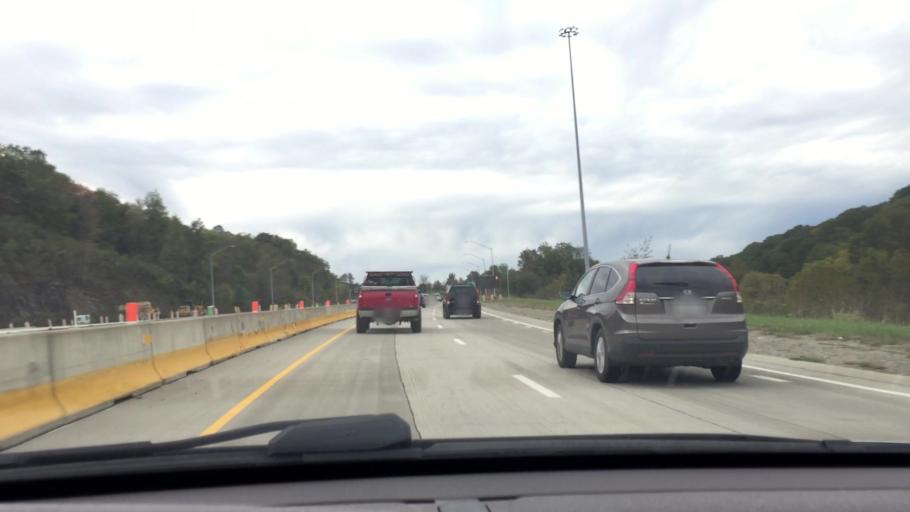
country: US
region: Pennsylvania
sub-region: Allegheny County
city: Enlow
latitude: 40.4694
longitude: -80.2057
